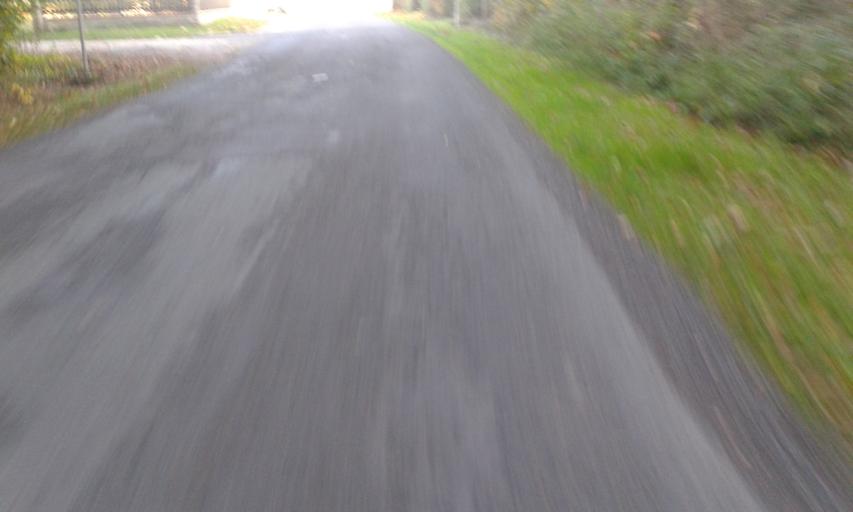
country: FR
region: Centre
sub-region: Departement du Loir-et-Cher
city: Ouzouer-le-Marche
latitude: 47.8541
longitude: 1.4457
